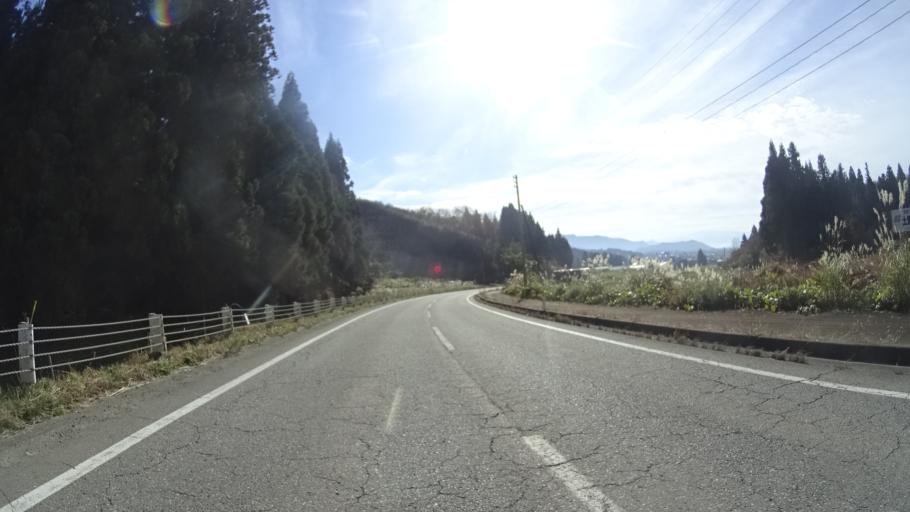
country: JP
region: Niigata
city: Muikamachi
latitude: 37.1897
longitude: 138.9816
